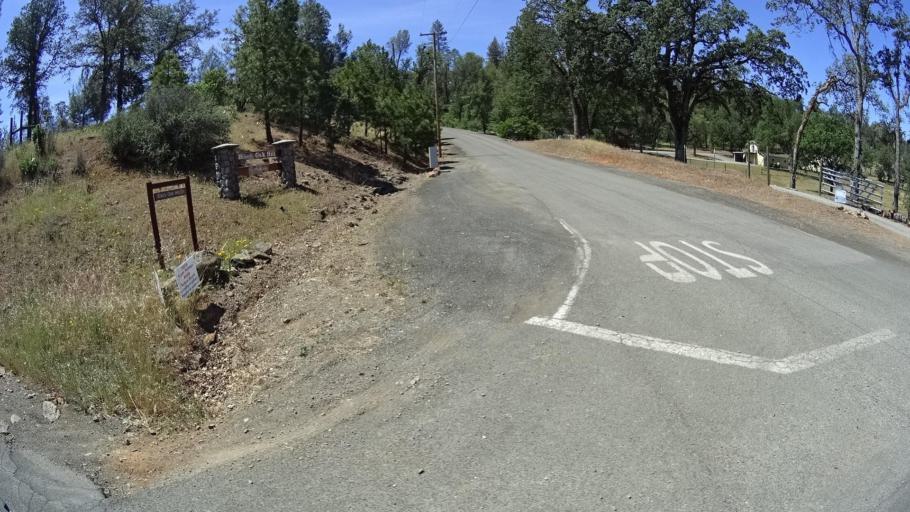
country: US
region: California
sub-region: Lake County
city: Middletown
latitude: 38.7515
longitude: -122.5968
